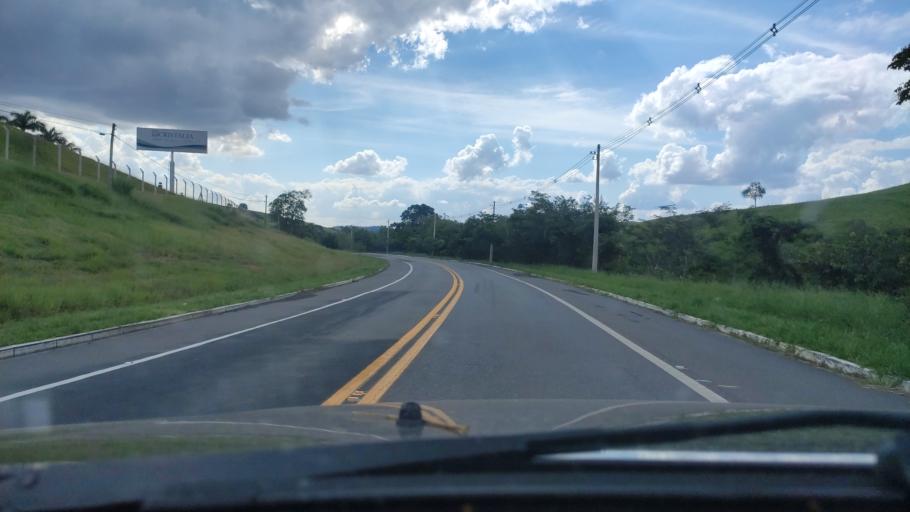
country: BR
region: Sao Paulo
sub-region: Aguas De Lindoia
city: Aguas de Lindoia
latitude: -22.4684
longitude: -46.7162
